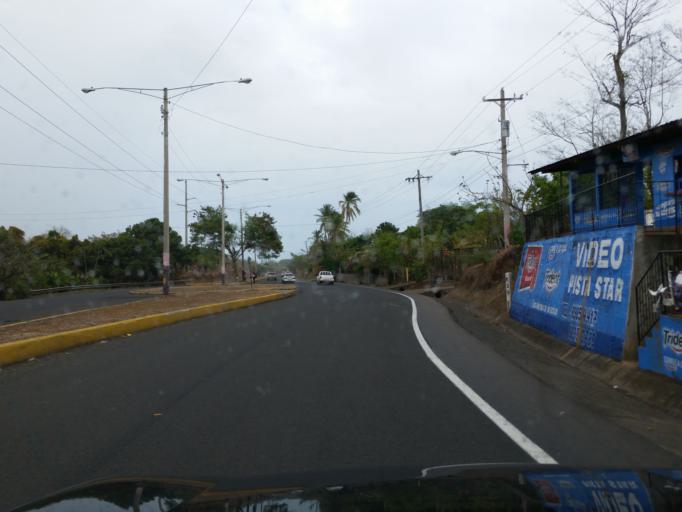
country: NI
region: Granada
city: Granada
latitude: 11.9672
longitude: -86.0137
